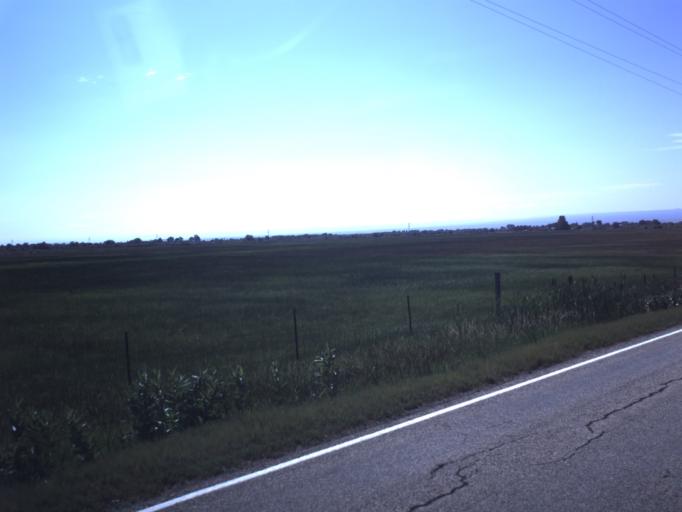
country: US
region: Utah
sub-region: Duchesne County
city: Duchesne
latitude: 40.3407
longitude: -110.2752
